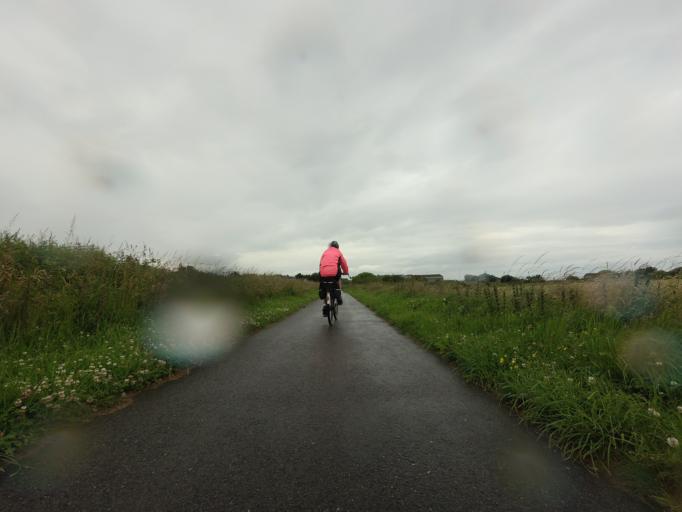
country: GB
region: Scotland
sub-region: Moray
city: Buckie
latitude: 57.6810
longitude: -2.9430
